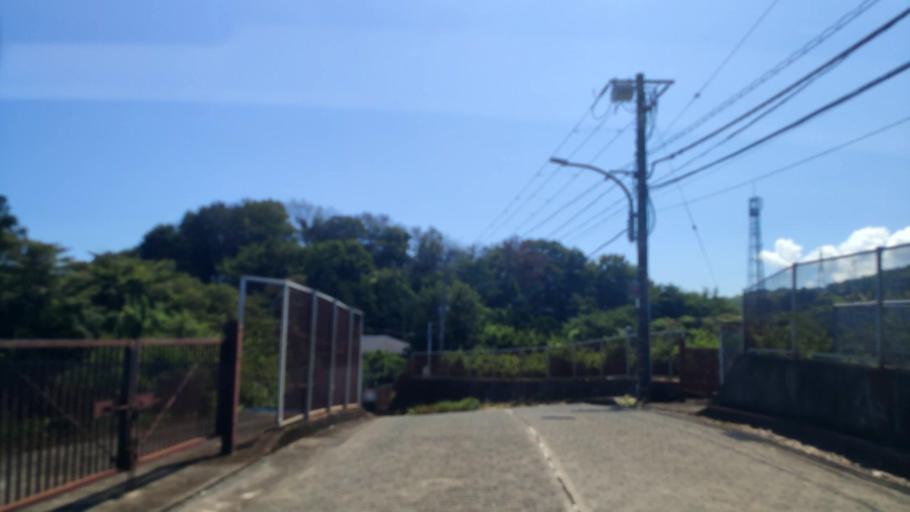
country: JP
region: Kanagawa
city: Odawara
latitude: 35.2496
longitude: 139.1347
